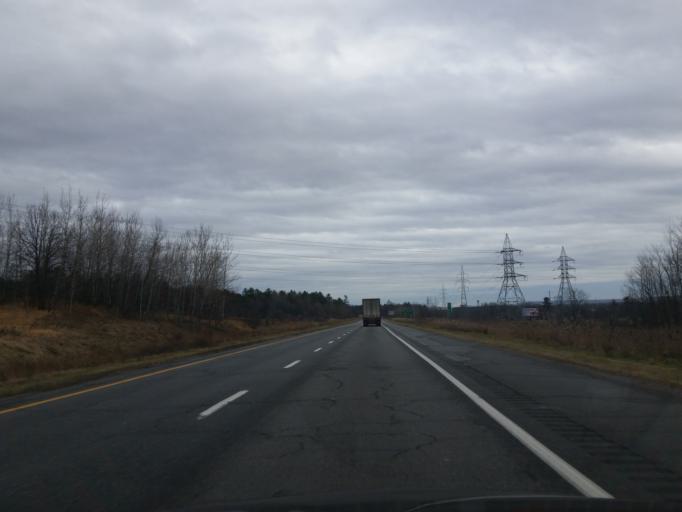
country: CA
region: Ontario
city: Clarence-Rockland
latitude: 45.5414
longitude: -75.4665
